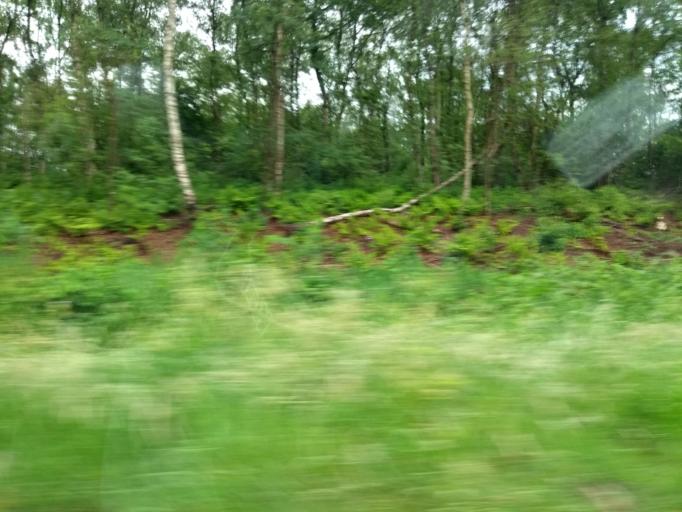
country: NL
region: Overijssel
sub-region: Gemeente Twenterand
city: Westerhaar-Vriezenveensewijk
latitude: 52.4360
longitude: 6.6295
